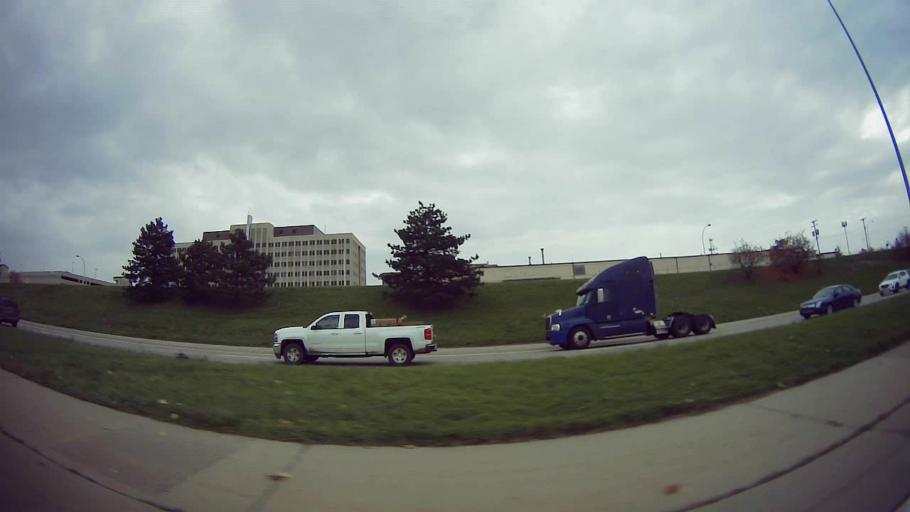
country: US
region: Michigan
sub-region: Macomb County
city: Center Line
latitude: 42.4927
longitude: -83.0455
